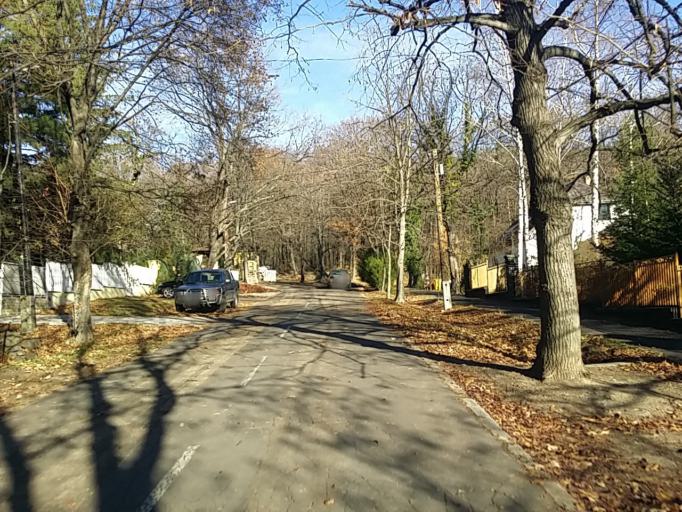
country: HU
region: Heves
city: Gyongyossolymos
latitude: 47.8340
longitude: 19.9649
